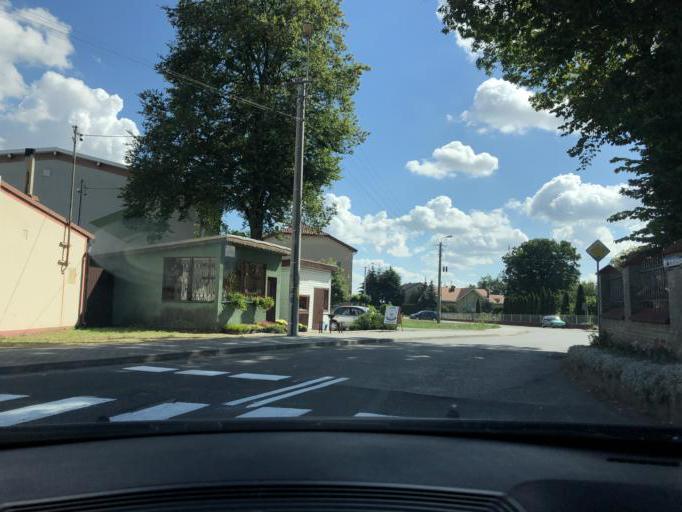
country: PL
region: Lodz Voivodeship
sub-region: Powiat wieruszowski
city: Czastary
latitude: 51.2588
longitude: 18.3213
